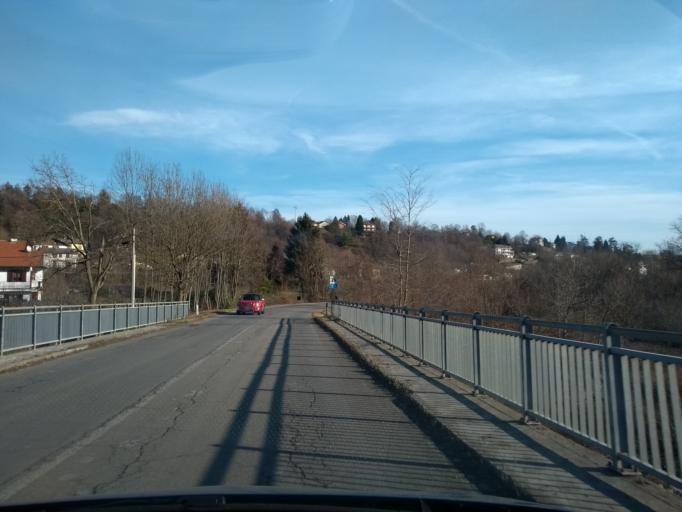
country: IT
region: Piedmont
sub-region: Provincia di Torino
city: Lanzo Torinese
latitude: 45.2814
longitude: 7.4750
